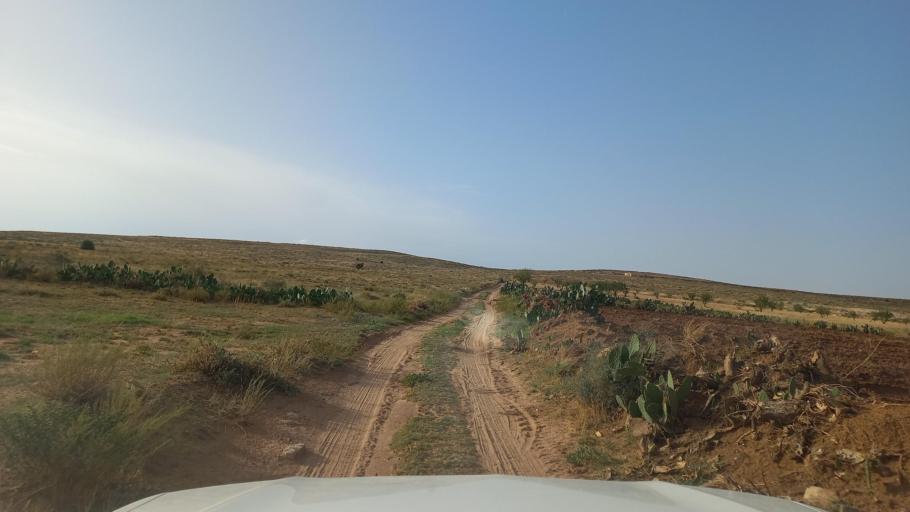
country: TN
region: Al Qasrayn
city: Kasserine
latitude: 35.3585
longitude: 8.8412
